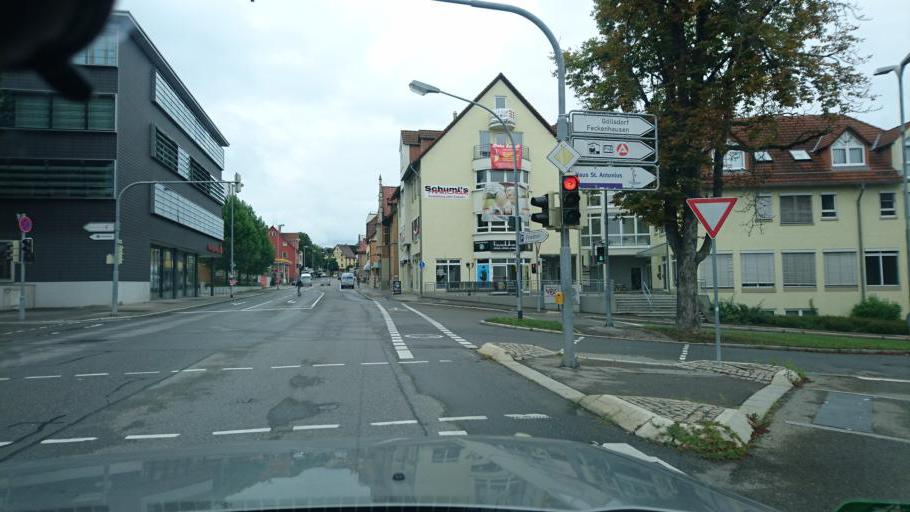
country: DE
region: Baden-Wuerttemberg
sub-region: Freiburg Region
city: Rottweil
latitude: 48.1617
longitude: 8.6355
